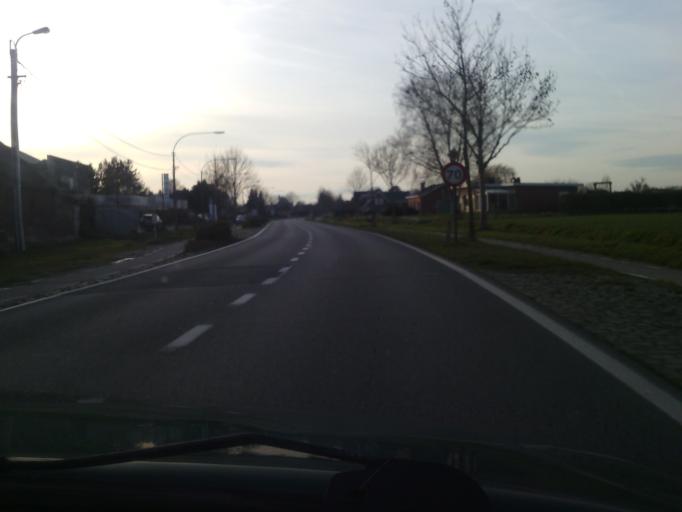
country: BE
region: Flanders
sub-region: Provincie Oost-Vlaanderen
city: Wetteren
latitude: 51.0465
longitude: 3.9235
